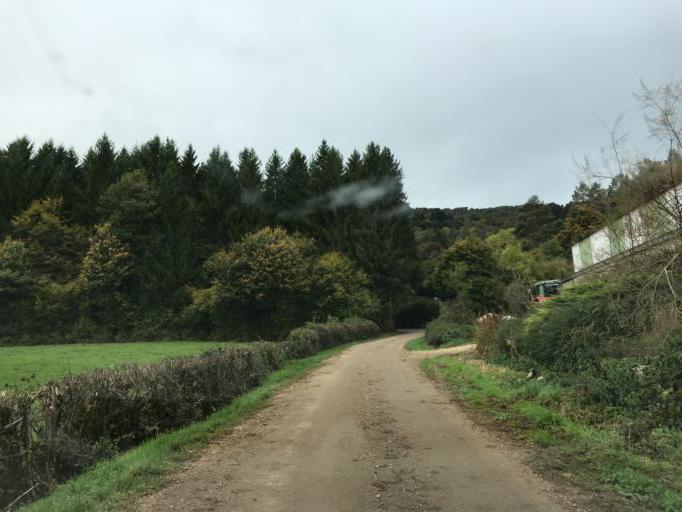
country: FR
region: Franche-Comte
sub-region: Departement du Jura
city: Arinthod
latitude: 46.4482
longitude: 5.5248
